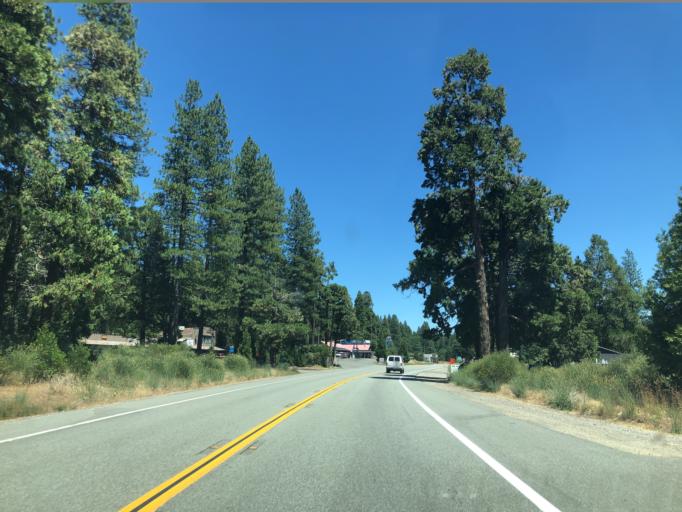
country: US
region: California
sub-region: Shasta County
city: Shingletown
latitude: 40.4917
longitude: -121.8911
